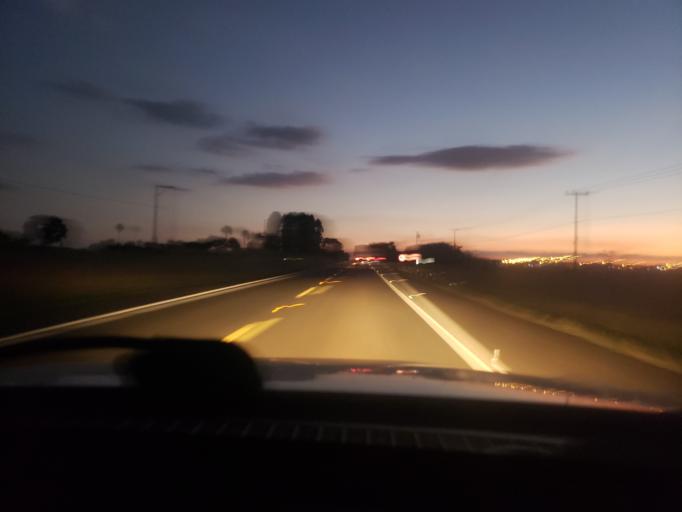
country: BR
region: Sao Paulo
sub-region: Conchal
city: Conchal
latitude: -22.3285
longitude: -47.1493
